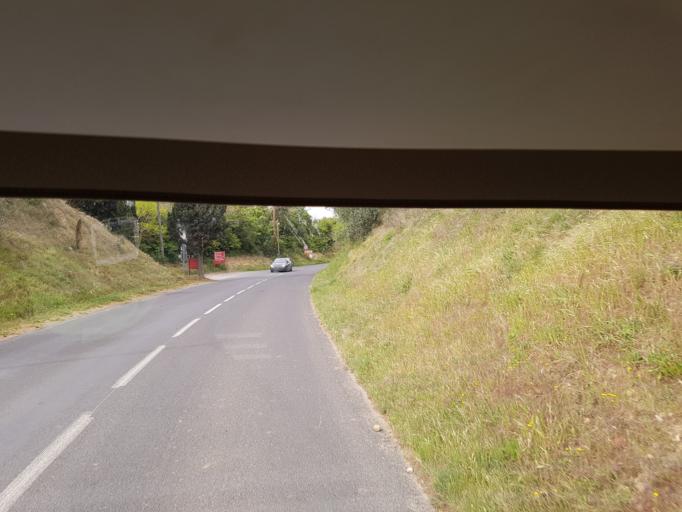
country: FR
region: Languedoc-Roussillon
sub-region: Departement de l'Aude
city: Fleury
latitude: 43.2243
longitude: 3.1318
